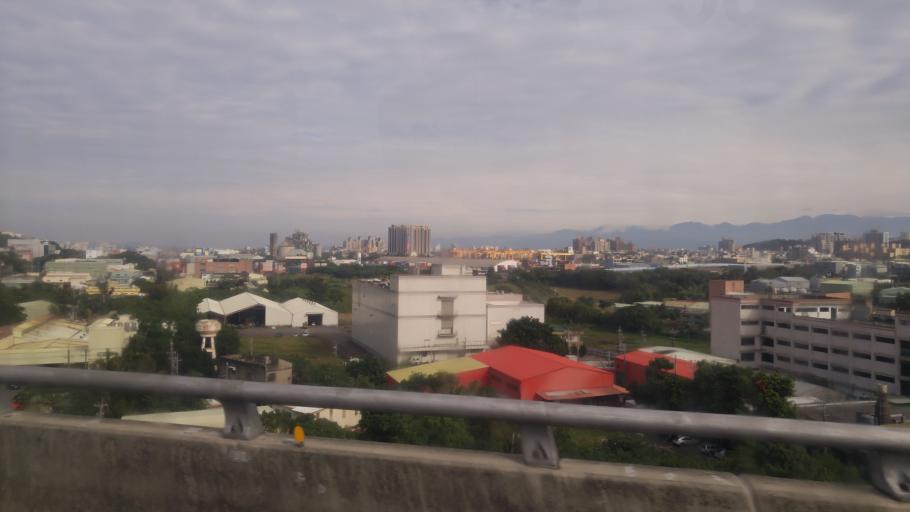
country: TW
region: Taiwan
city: Daxi
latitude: 24.9164
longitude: 121.1673
